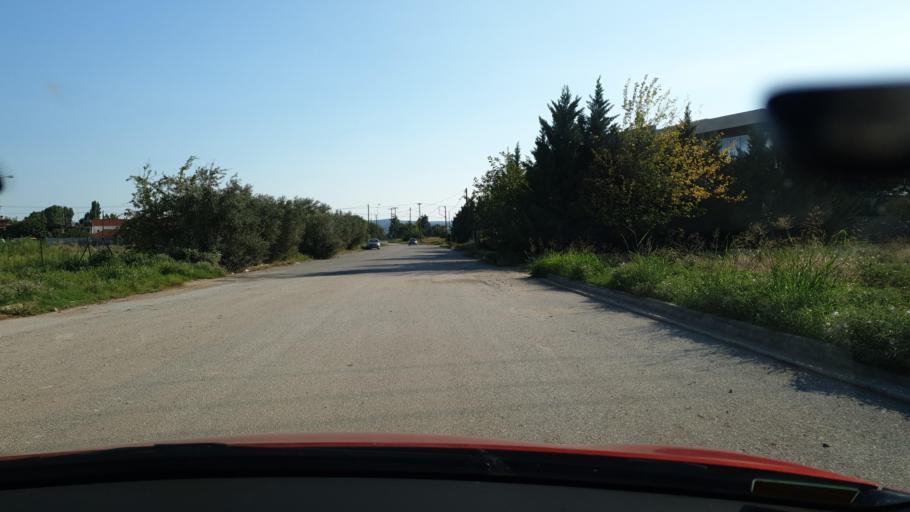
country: GR
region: Central Macedonia
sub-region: Nomos Thessalonikis
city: Thermi
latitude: 40.5410
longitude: 23.0122
